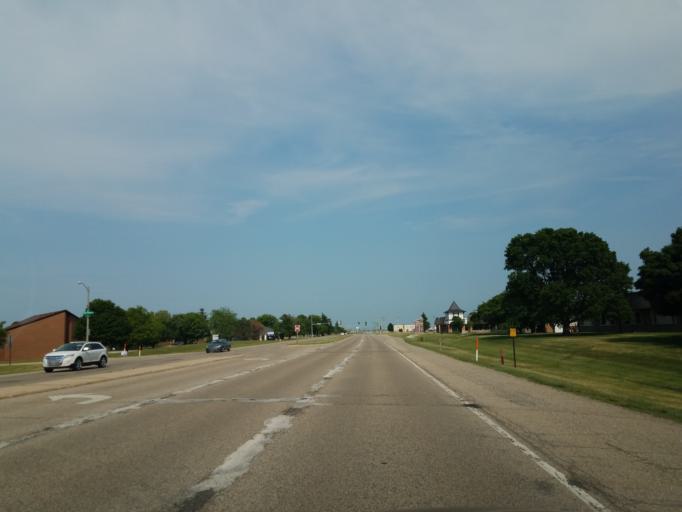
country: US
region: Illinois
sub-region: McLean County
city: Bloomington
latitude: 40.4883
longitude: -88.9317
